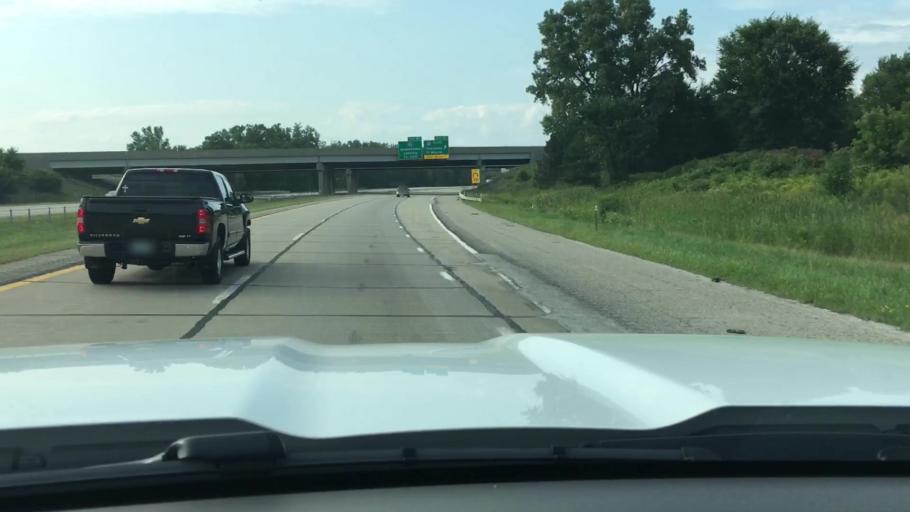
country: US
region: Michigan
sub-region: Eaton County
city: Dimondale
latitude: 42.6880
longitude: -84.6661
